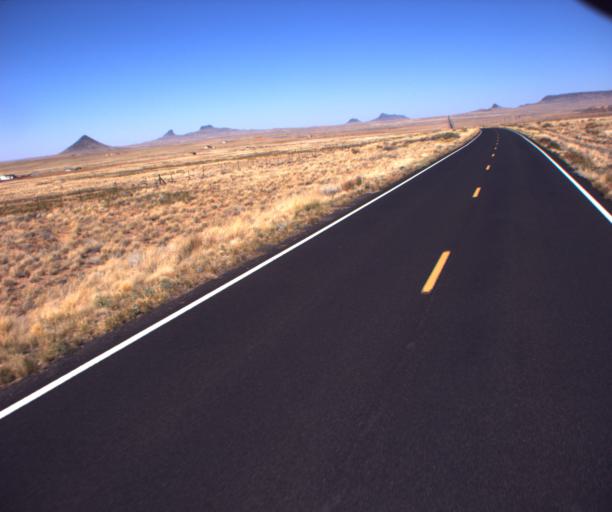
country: US
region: Arizona
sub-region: Navajo County
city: Dilkon
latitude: 35.3060
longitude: -110.4228
